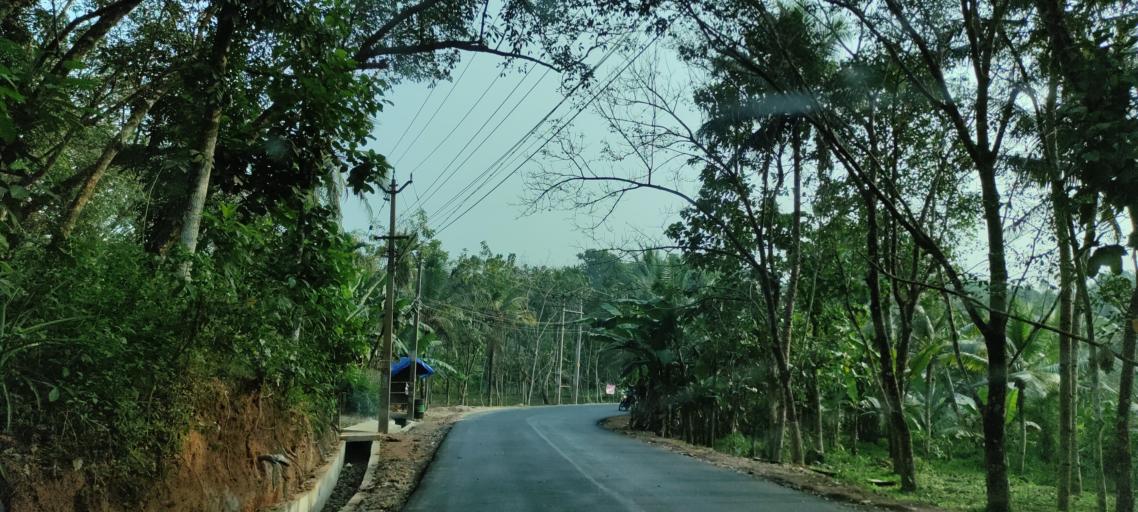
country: IN
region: Kerala
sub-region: Pattanamtitta
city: Adur
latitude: 9.1108
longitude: 76.7289
